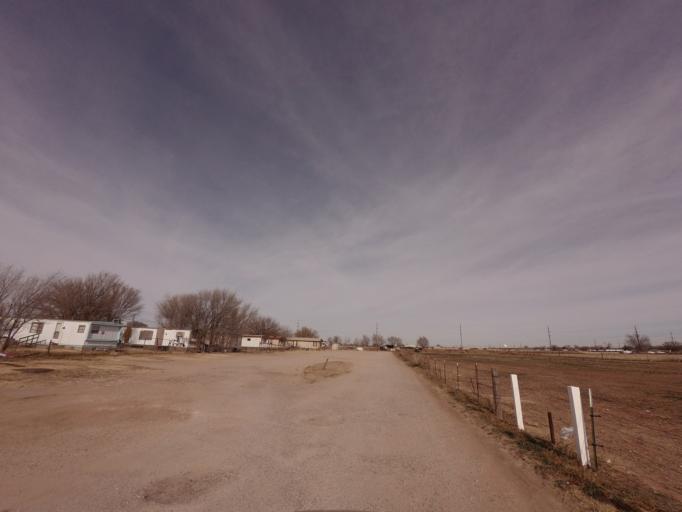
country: US
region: New Mexico
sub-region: Curry County
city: Clovis
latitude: 34.4104
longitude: -103.2342
